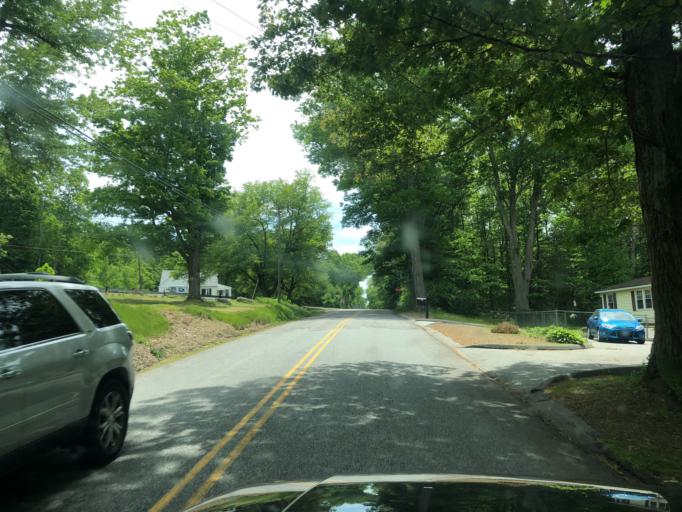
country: US
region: Connecticut
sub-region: Windham County
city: North Grosvenor Dale
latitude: 41.9831
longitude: -71.8921
